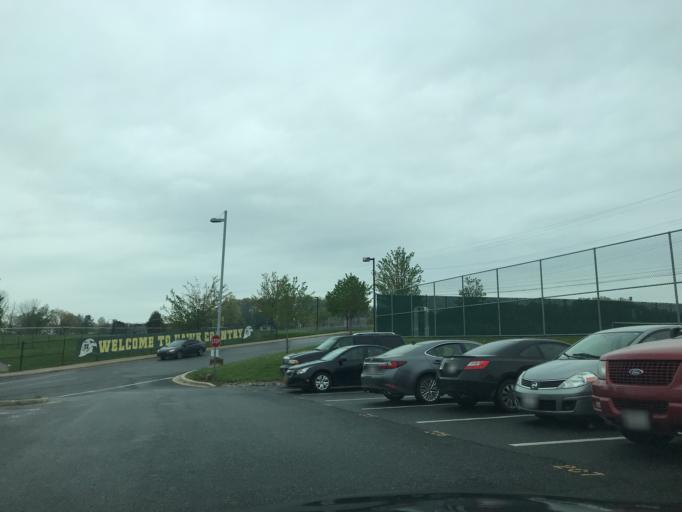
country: US
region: Pennsylvania
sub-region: York County
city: Susquehanna Trails
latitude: 39.6756
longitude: -76.4025
